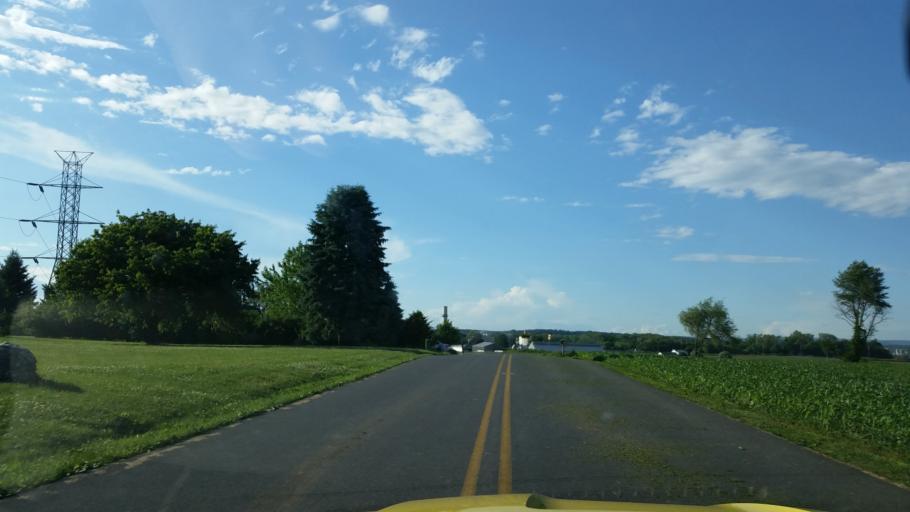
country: US
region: Pennsylvania
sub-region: Lebanon County
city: Avon
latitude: 40.3424
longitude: -76.3628
